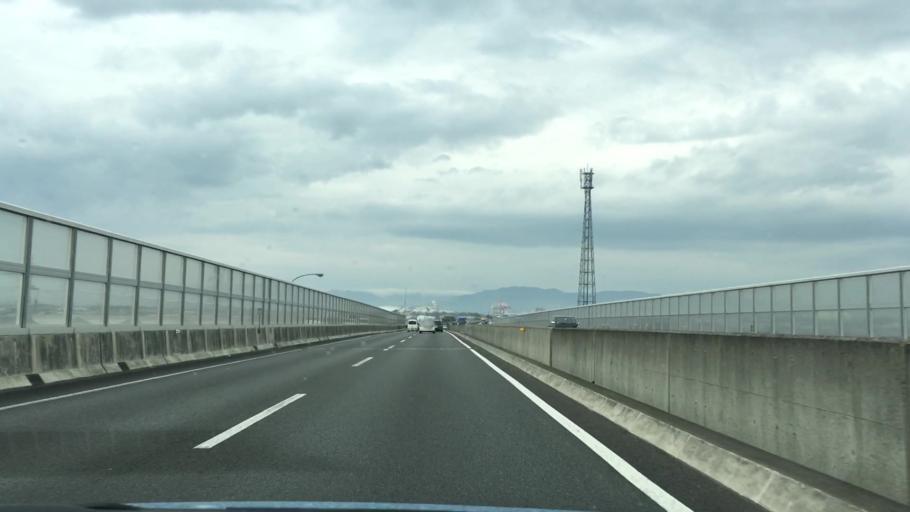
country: JP
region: Aichi
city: Toyohashi
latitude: 34.7419
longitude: 137.3406
